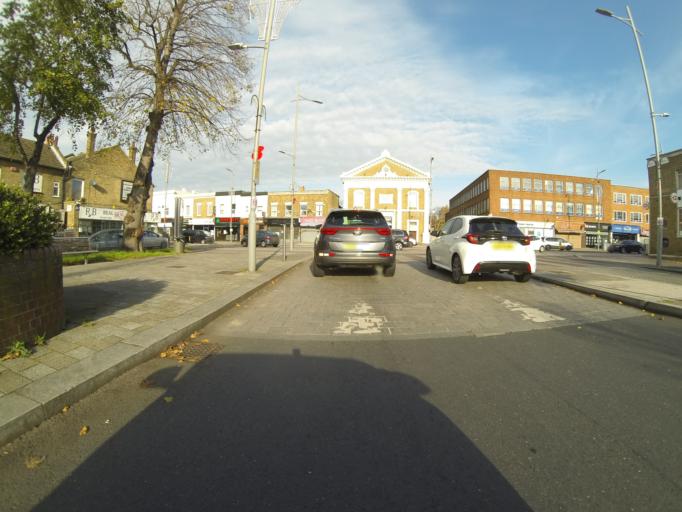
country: GB
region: England
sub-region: Greater London
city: Bexleyheath
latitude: 51.4571
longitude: 0.1385
